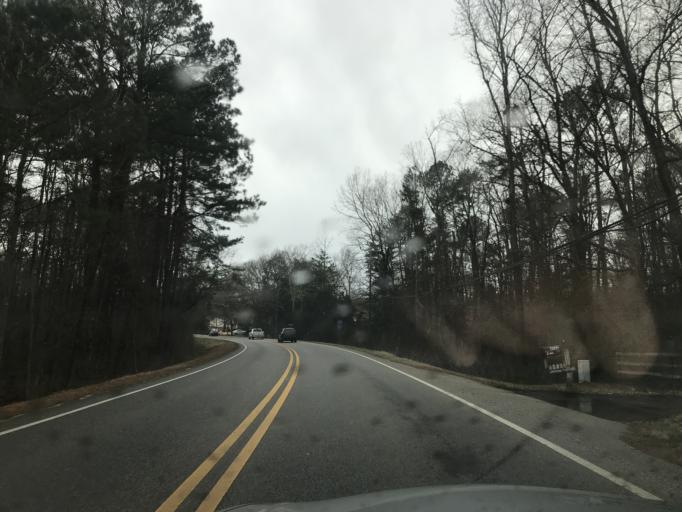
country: US
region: Alabama
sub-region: Shelby County
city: Indian Springs Village
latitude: 33.3739
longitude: -86.7247
